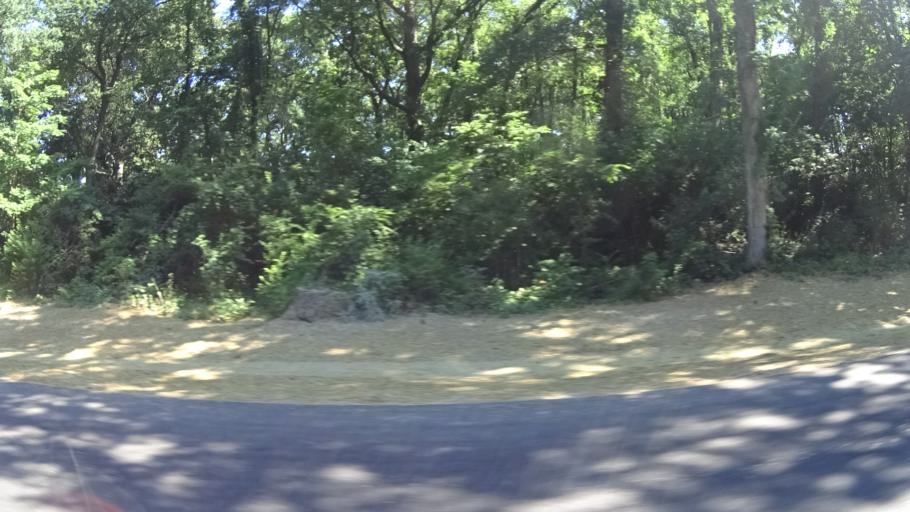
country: US
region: Ohio
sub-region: Erie County
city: Huron
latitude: 41.3950
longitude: -82.6373
